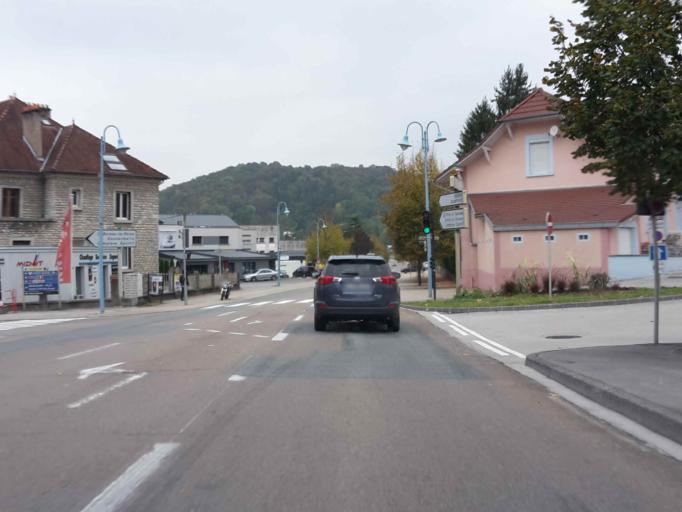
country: FR
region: Franche-Comte
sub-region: Departement du Doubs
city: Baume-les-Dames
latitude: 47.3508
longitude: 6.3606
